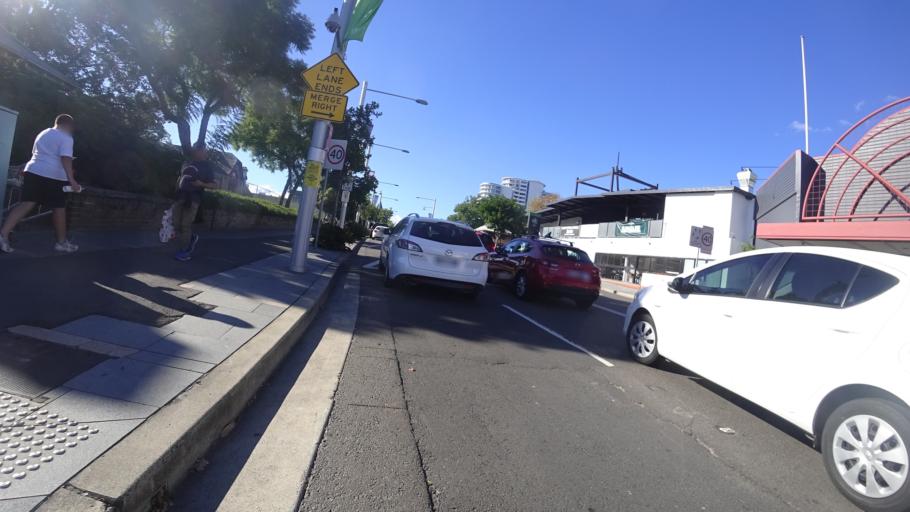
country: AU
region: New South Wales
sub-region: The Hills Shire
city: Castle Hill
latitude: -33.7337
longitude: 151.0040
